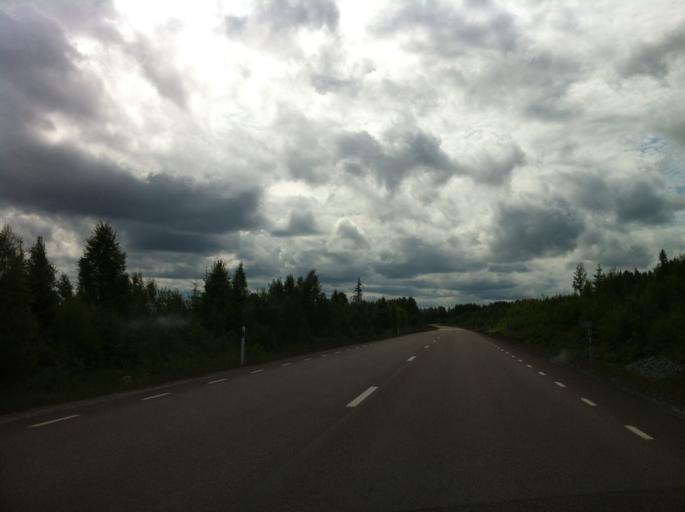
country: SE
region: Vaermland
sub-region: Sunne Kommun
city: Sunne
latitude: 59.7511
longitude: 13.1203
